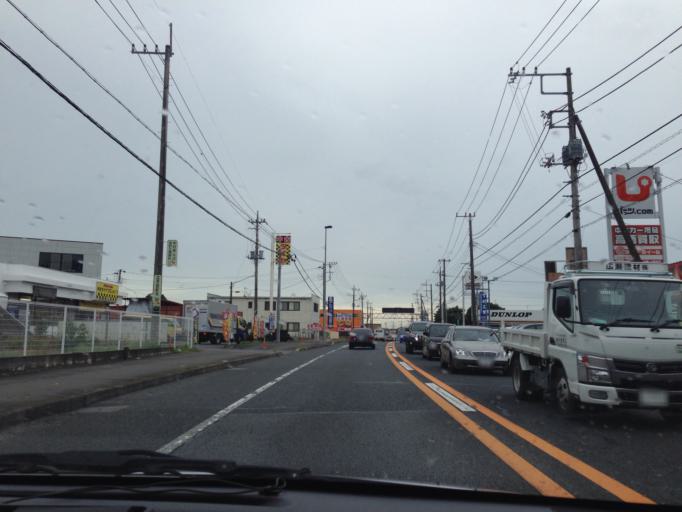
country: JP
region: Ibaraki
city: Naka
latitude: 36.0178
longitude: 140.1587
